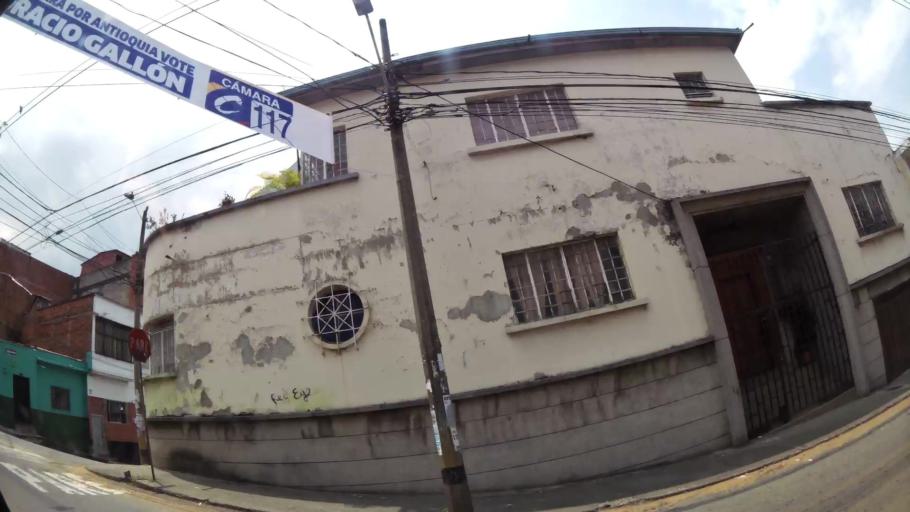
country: CO
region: Antioquia
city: Medellin
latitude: 6.2556
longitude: -75.5590
